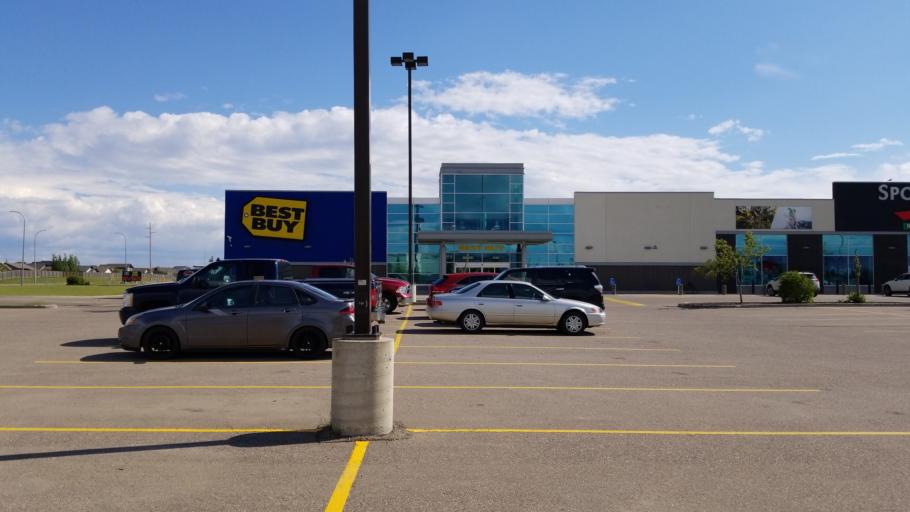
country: CA
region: Saskatchewan
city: Lloydminster
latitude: 53.2766
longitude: -110.0556
